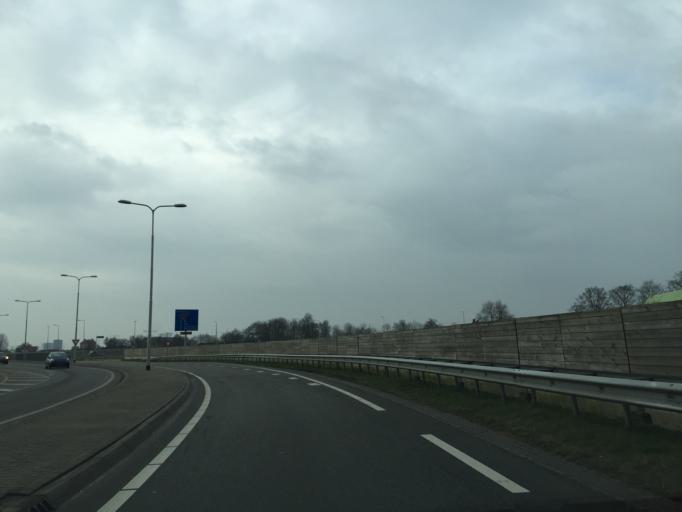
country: NL
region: South Holland
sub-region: Gemeente Lansingerland
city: Bleiswijk
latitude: 52.0011
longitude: 4.5936
